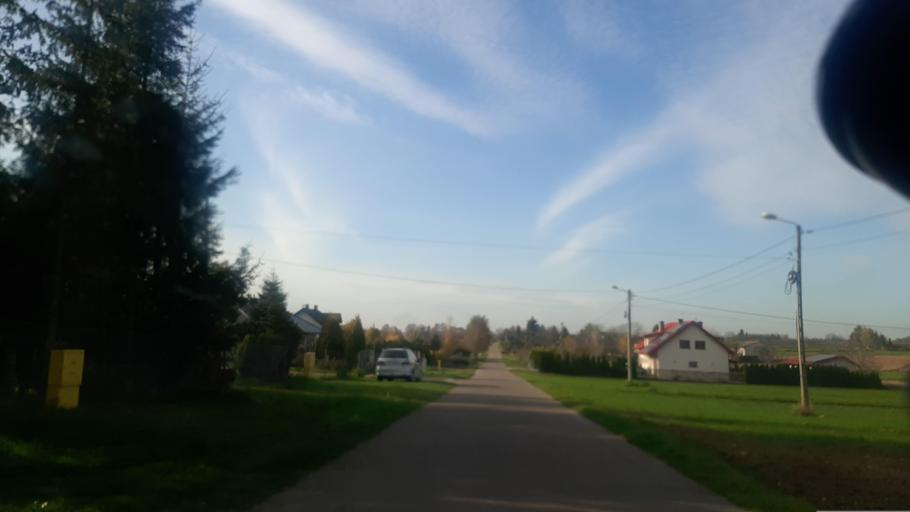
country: PL
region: Lublin Voivodeship
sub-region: Powiat pulawski
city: Markuszow
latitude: 51.3635
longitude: 22.2894
